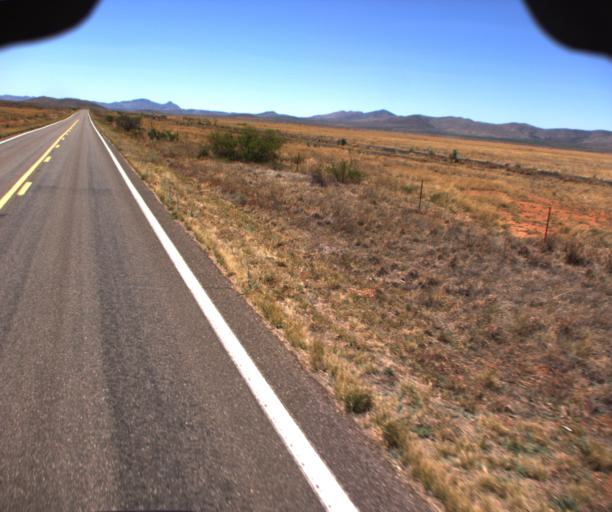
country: US
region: Arizona
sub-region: Cochise County
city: Douglas
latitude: 31.5988
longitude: -109.2340
